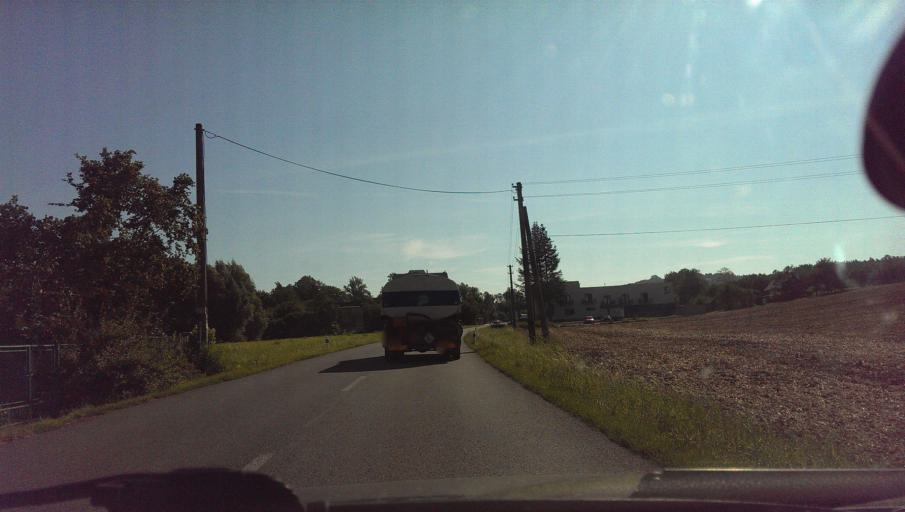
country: CZ
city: Frycovice
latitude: 49.6837
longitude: 18.2409
